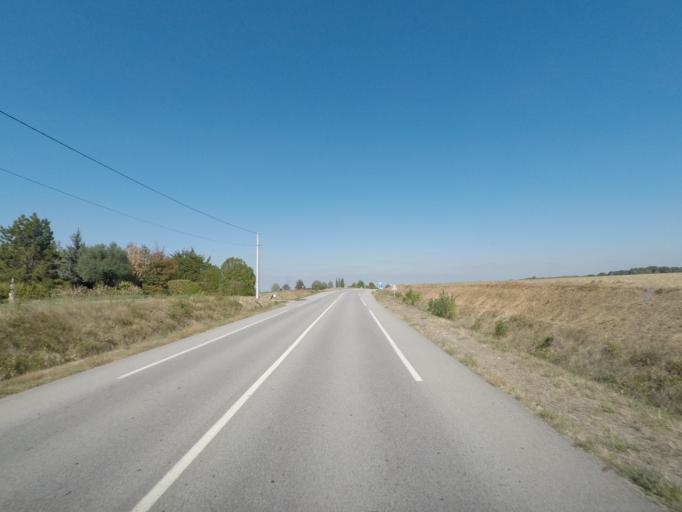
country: FR
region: Rhone-Alpes
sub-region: Departement de la Drome
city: Montmeyran
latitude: 44.8404
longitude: 5.0095
